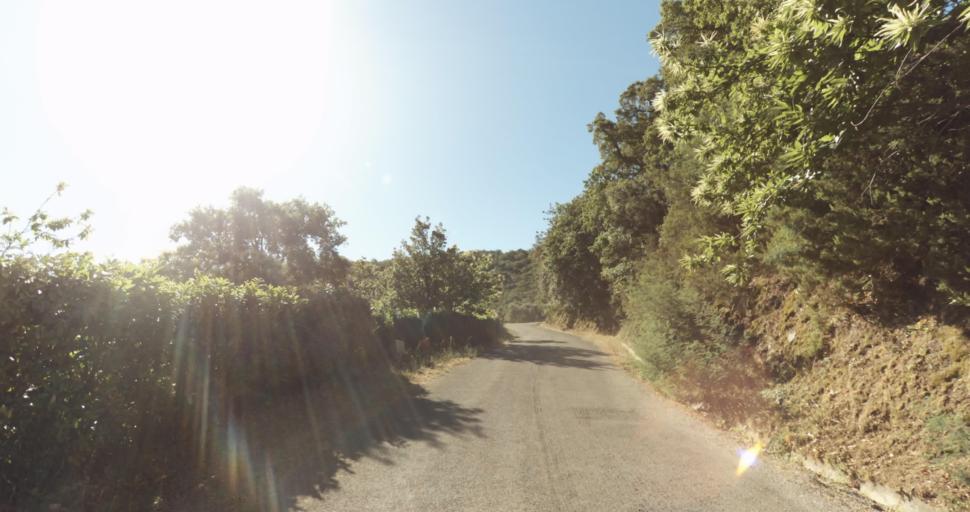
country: FR
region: Provence-Alpes-Cote d'Azur
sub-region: Departement du Var
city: Gassin
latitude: 43.2218
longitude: 6.5968
